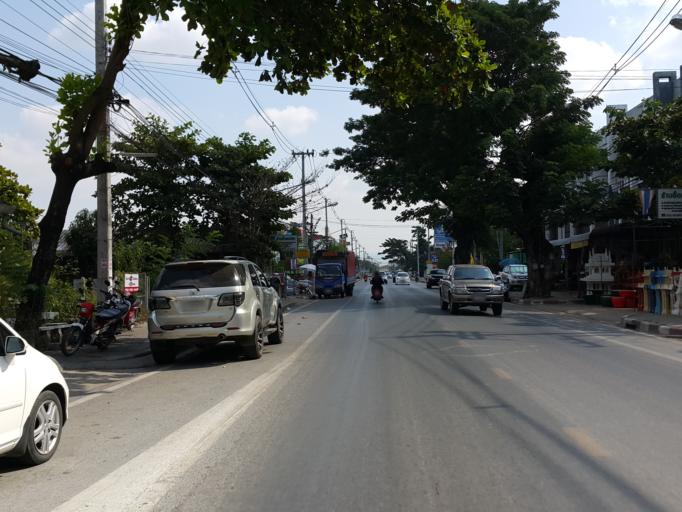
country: TH
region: Chiang Mai
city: San Kamphaeng
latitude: 18.7484
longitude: 99.1134
